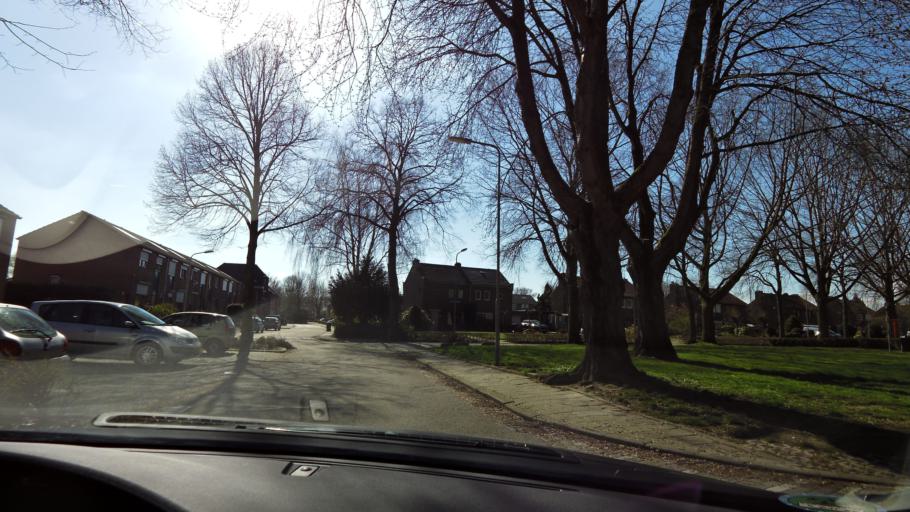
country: NL
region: Limburg
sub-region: Gemeente Sittard-Geleen
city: Sittard
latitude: 50.9872
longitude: 5.8580
